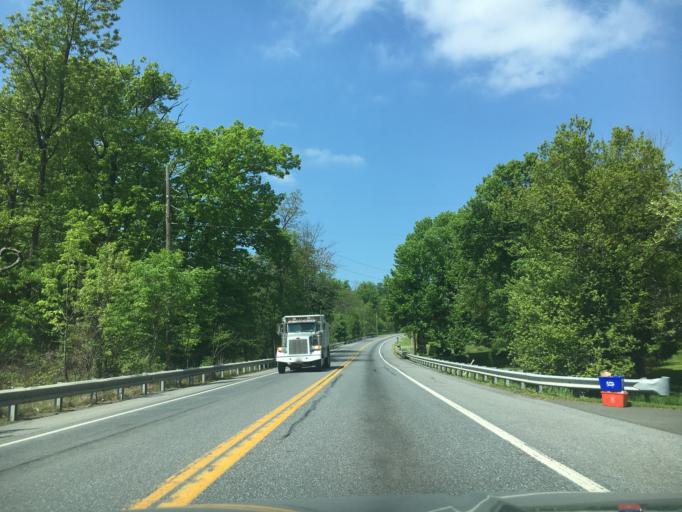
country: US
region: Pennsylvania
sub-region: Berks County
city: New Berlinville
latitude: 40.3622
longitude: -75.6869
